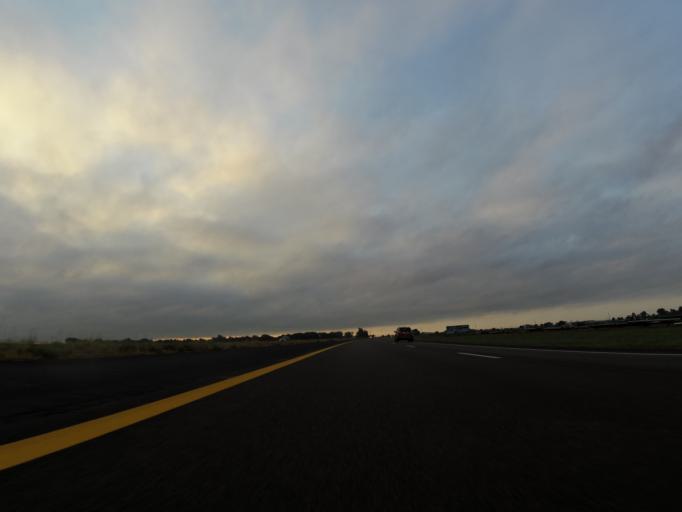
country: US
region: Kansas
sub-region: Sedgwick County
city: Colwich
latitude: 37.8728
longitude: -97.6274
